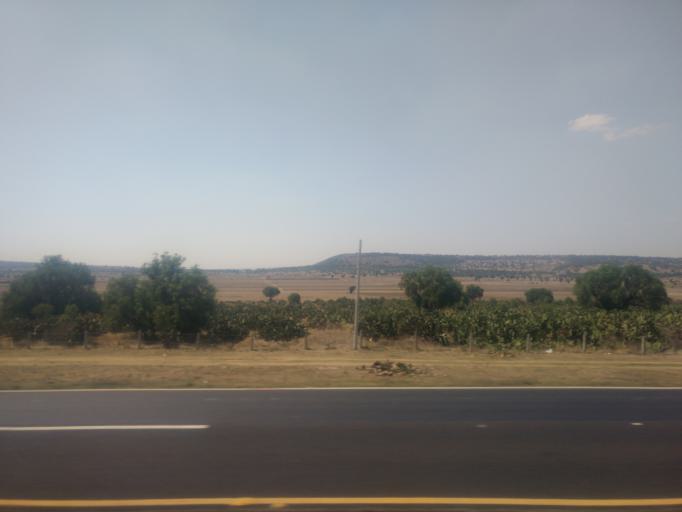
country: MX
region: Morelos
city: Nopaltepec
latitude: 19.8186
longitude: -98.7130
